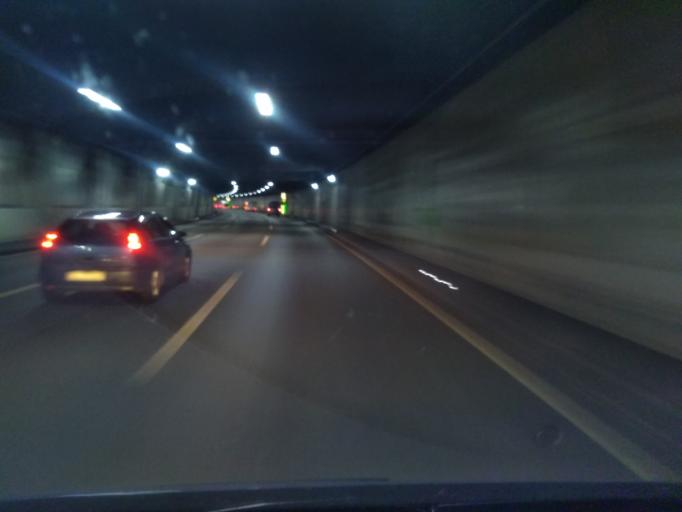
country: CH
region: Basel-Landschaft
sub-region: Bezirk Arlesheim
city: Muttenz
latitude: 47.5311
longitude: 7.6621
